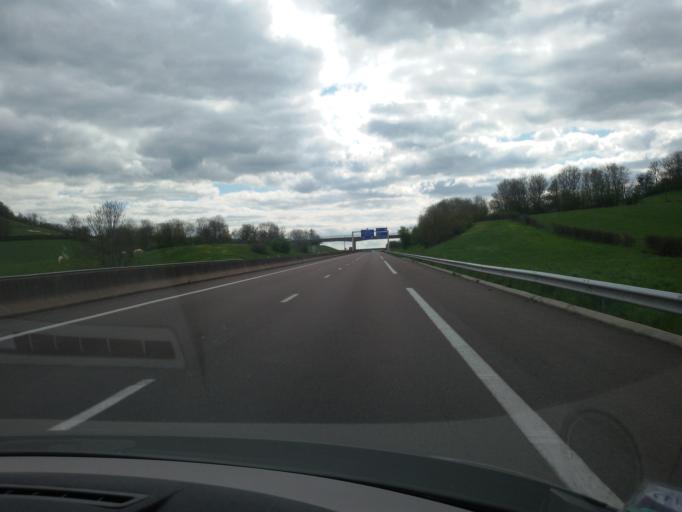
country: FR
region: Bourgogne
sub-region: Departement de la Cote-d'Or
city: Pouilly-en-Auxois
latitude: 47.2541
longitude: 4.5448
